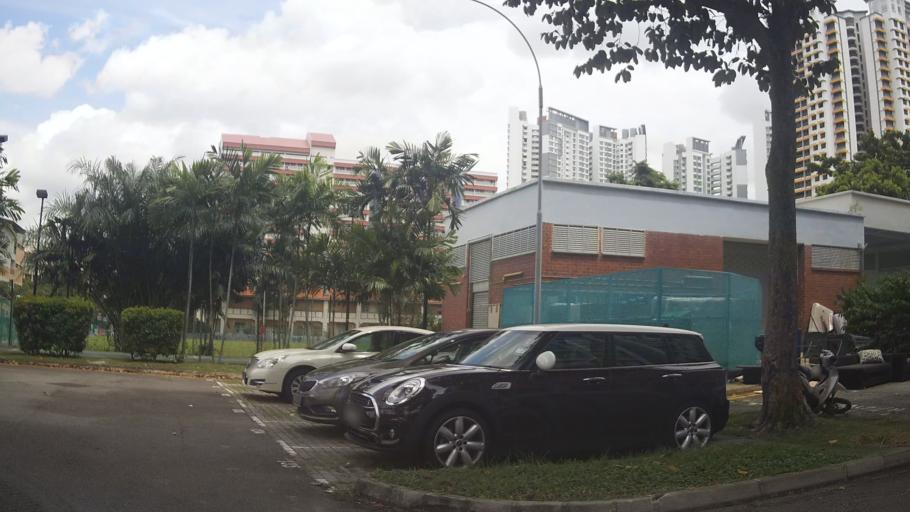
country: SG
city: Singapore
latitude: 1.3200
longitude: 103.8569
